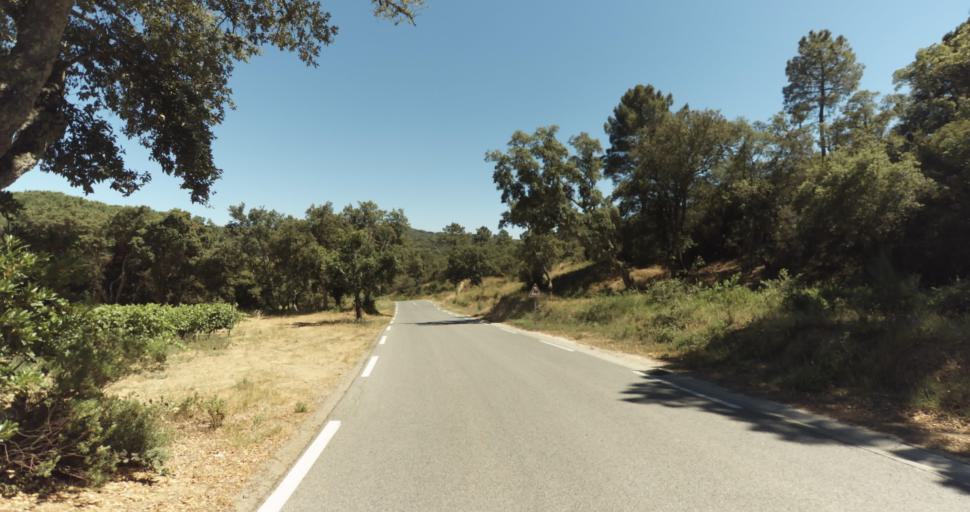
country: FR
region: Provence-Alpes-Cote d'Azur
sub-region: Departement du Var
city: Gassin
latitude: 43.2399
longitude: 6.5634
